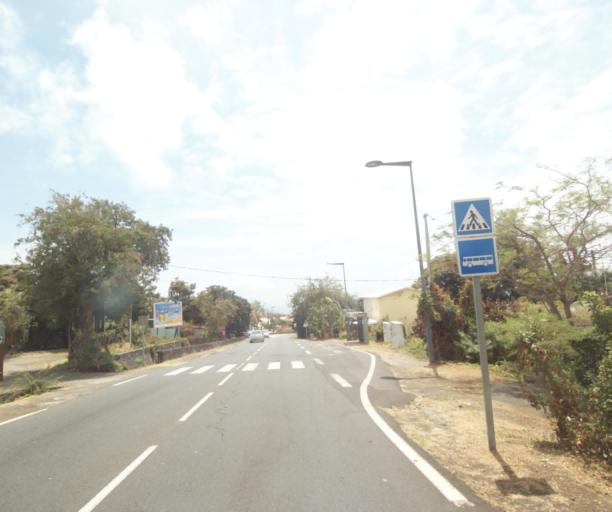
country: RE
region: Reunion
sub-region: Reunion
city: Saint-Paul
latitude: -21.0302
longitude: 55.2666
